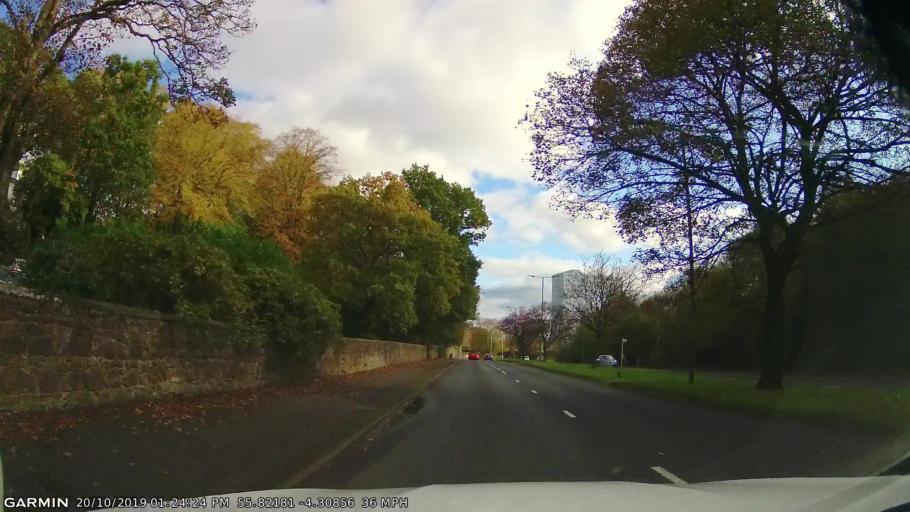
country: GB
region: Scotland
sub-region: East Renfrewshire
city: Giffnock
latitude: 55.8218
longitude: -4.3086
